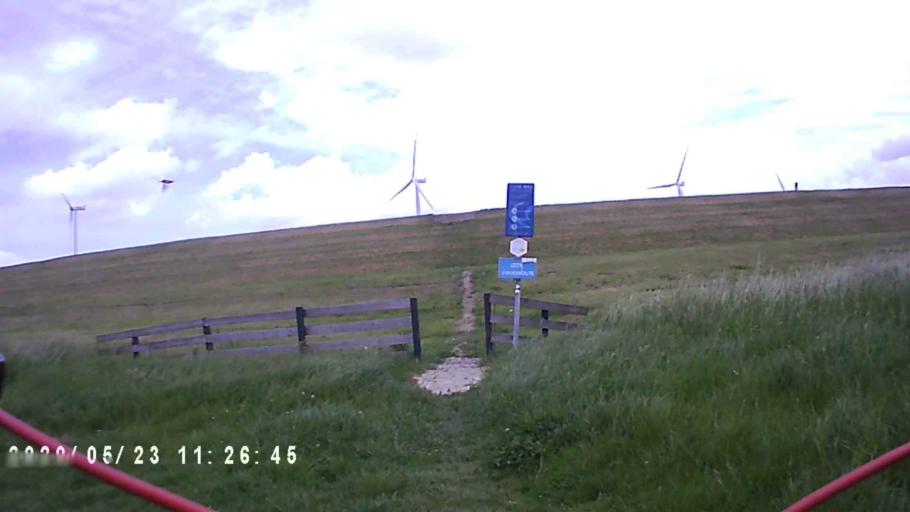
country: NL
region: Groningen
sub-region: Gemeente Delfzijl
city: Delfzijl
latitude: 53.3117
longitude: 6.9923
